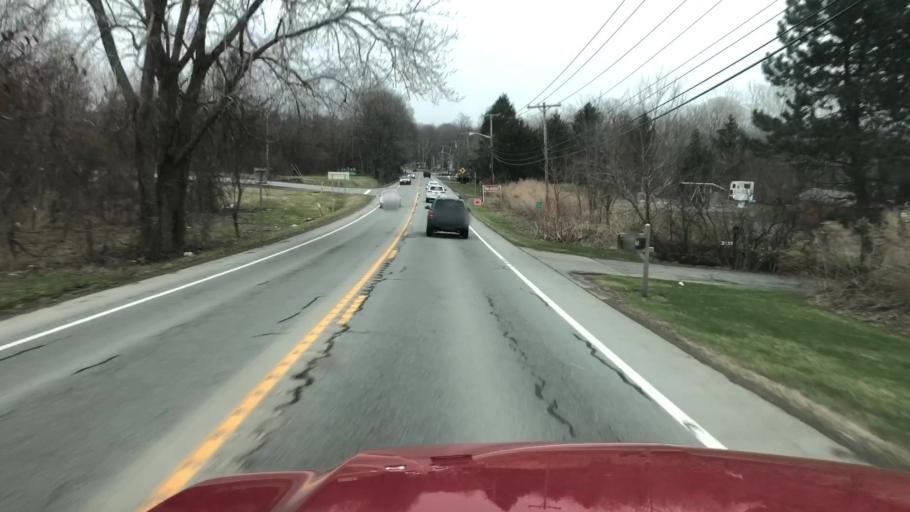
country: US
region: New York
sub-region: Monroe County
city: Fairport
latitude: 43.1309
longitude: -77.3784
